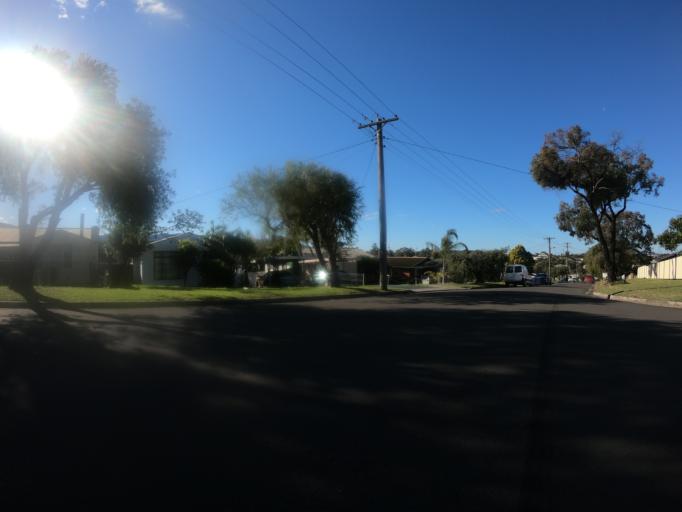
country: AU
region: New South Wales
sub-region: Wollongong
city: Cordeaux Heights
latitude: -34.4643
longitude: 150.8325
